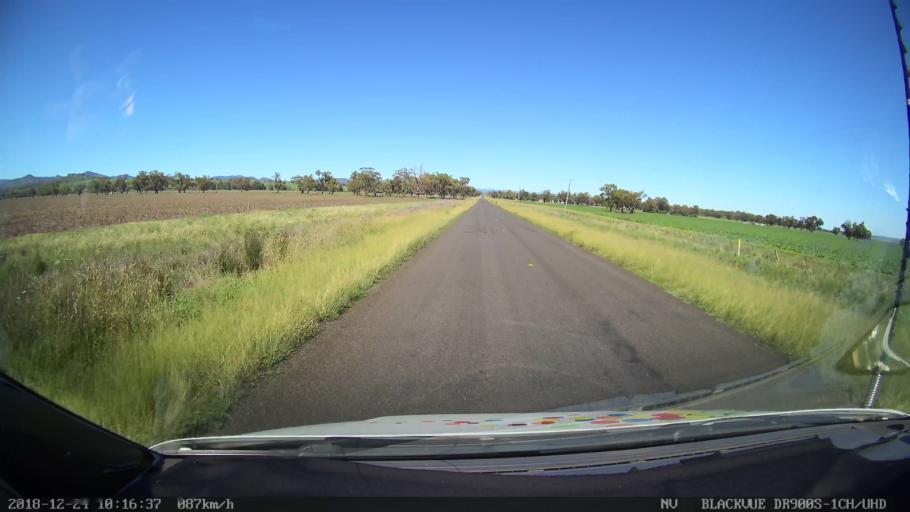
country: AU
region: New South Wales
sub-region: Liverpool Plains
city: Quirindi
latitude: -31.7169
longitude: 150.6036
